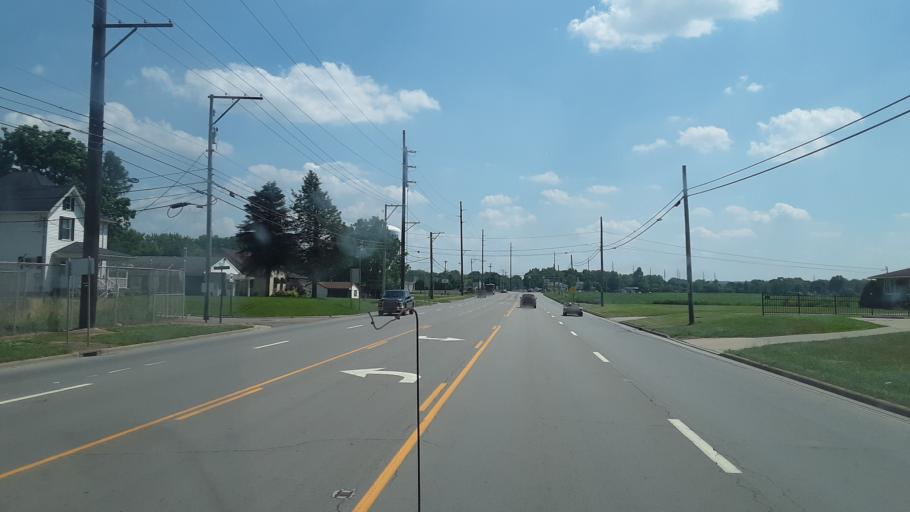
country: US
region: Ohio
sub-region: Stark County
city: Navarre
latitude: 40.7402
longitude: -81.5174
